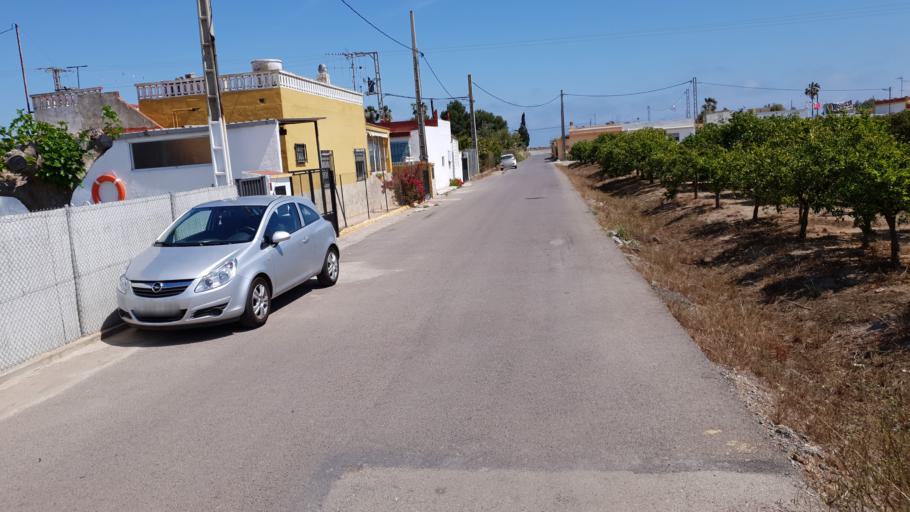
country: ES
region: Valencia
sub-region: Provincia de Castello
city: Burriana
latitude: 39.8589
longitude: -0.0874
